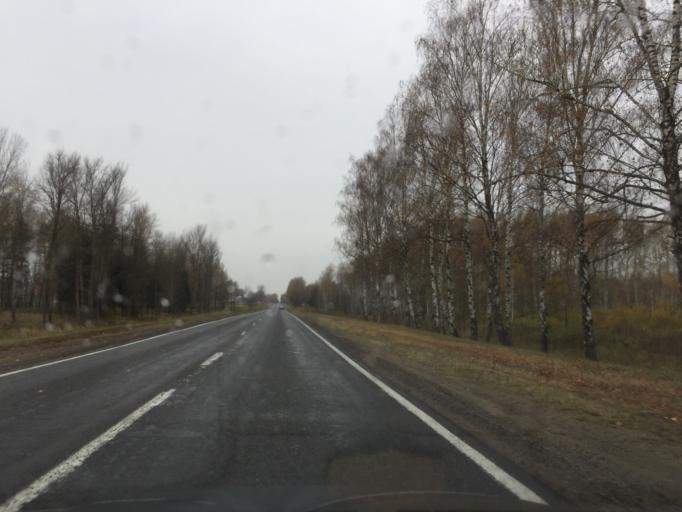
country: BY
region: Mogilev
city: Slawharad
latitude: 53.3451
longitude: 30.8111
